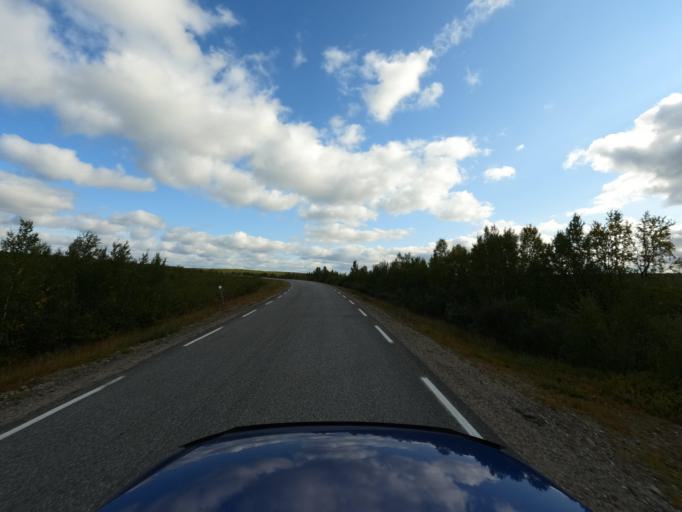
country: NO
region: Finnmark Fylke
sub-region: Porsanger
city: Lakselv
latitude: 69.3737
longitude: 24.4196
